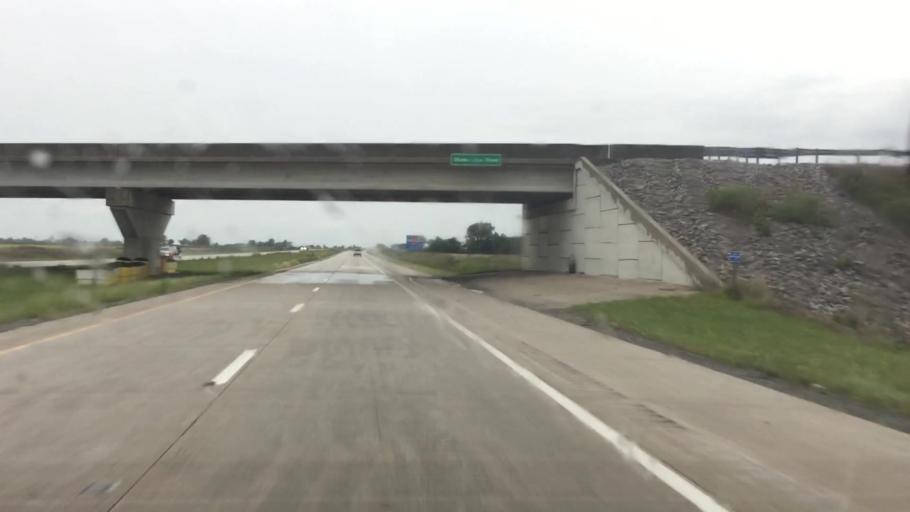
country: US
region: Ohio
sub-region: Paulding County
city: Antwerp
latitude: 41.1561
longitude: -84.7951
